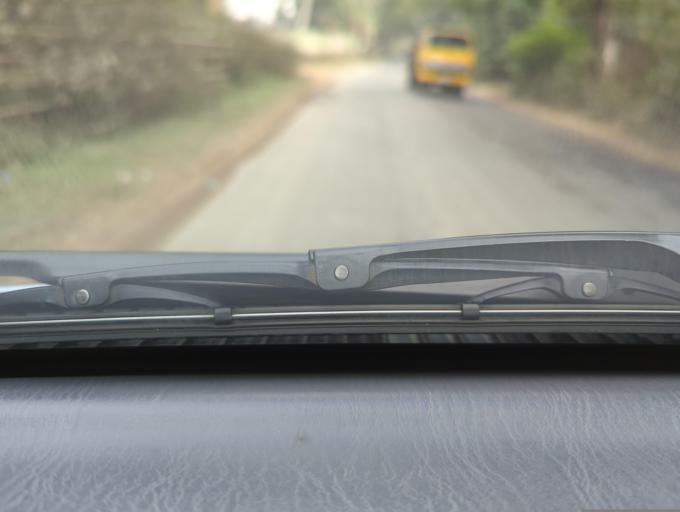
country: BD
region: Sylhet
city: Maulavi Bazar
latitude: 24.5048
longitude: 91.7349
